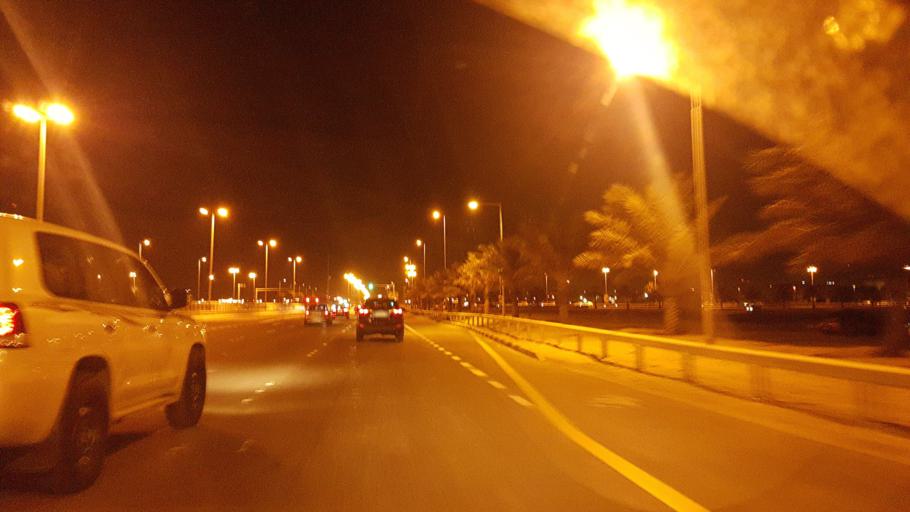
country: BH
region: Muharraq
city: Al Hadd
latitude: 26.2564
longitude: 50.6600
